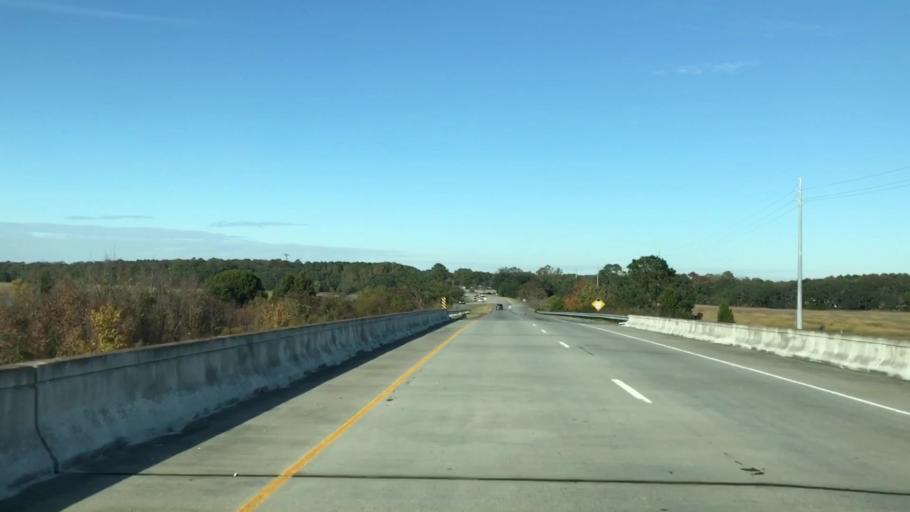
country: US
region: South Carolina
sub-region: Beaufort County
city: Laurel Bay
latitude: 32.5415
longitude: -80.7450
